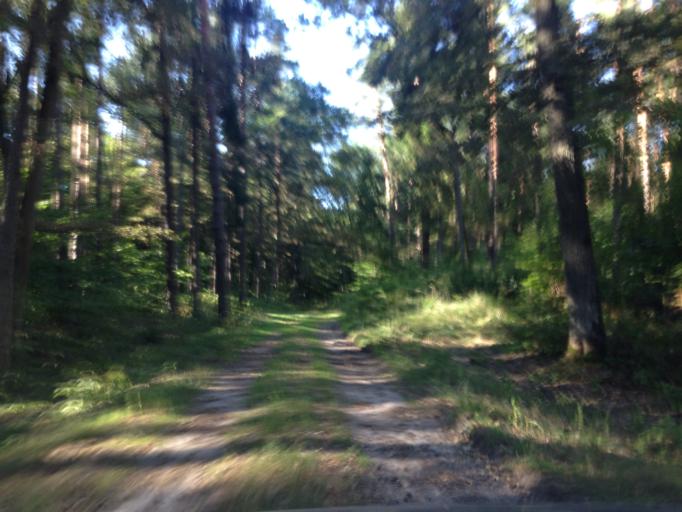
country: PL
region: Kujawsko-Pomorskie
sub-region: Powiat brodnicki
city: Gorzno
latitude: 53.1740
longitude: 19.6643
